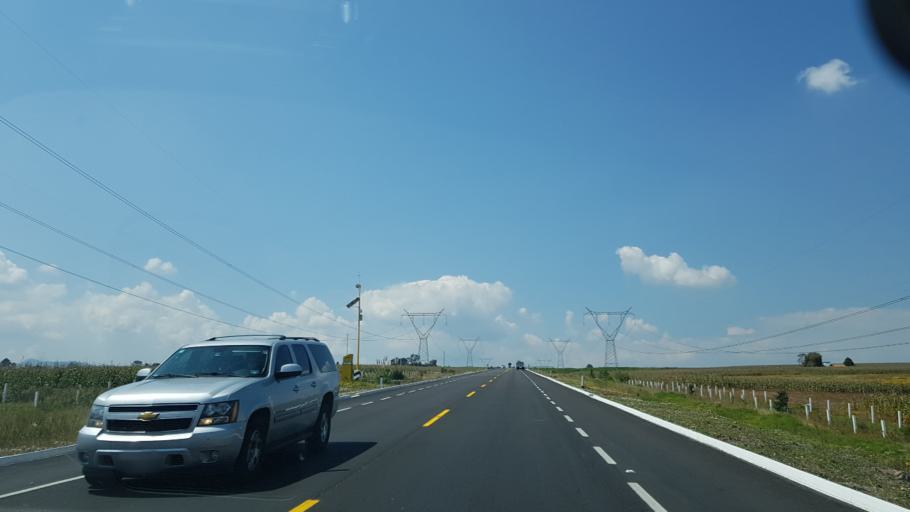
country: MX
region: Mexico
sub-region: Almoloya de Juarez
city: San Pedro de la Hortaliza (Ejido Almoloyan)
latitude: 19.3785
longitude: -99.8372
